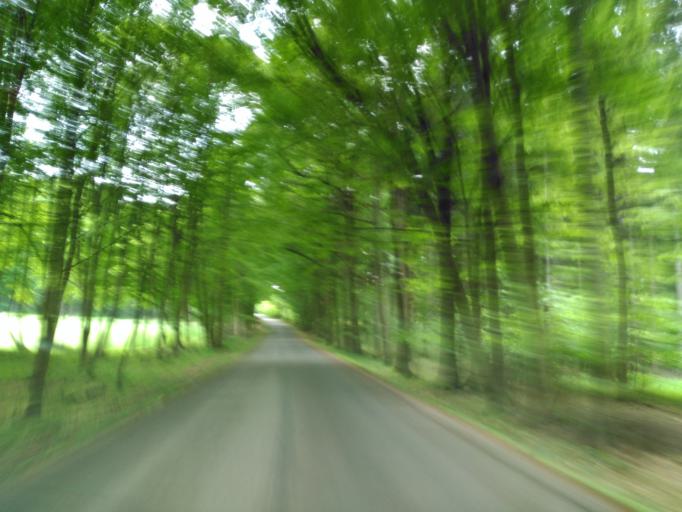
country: CZ
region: Central Bohemia
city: Zebrak
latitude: 49.9241
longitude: 13.8295
